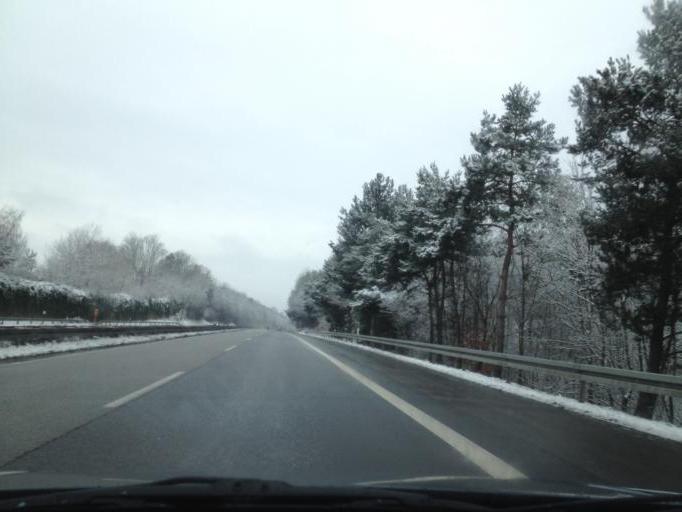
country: DE
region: Saarland
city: Neunkirchen
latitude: 49.3277
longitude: 7.2175
